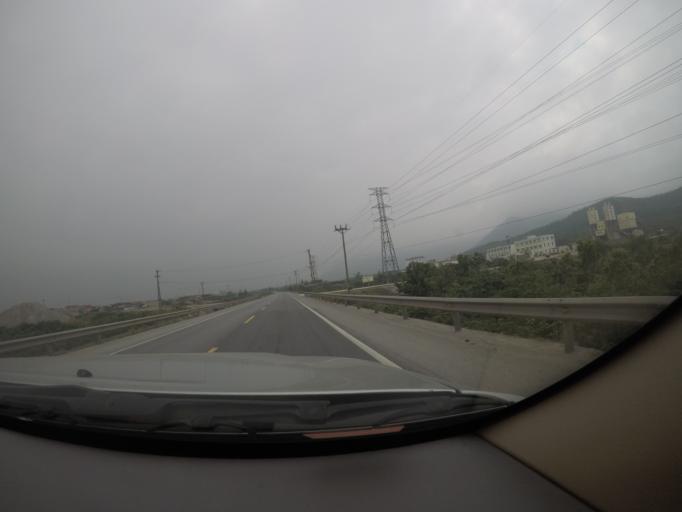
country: VN
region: Ha Tinh
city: Ky Anh
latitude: 18.0038
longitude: 106.4299
